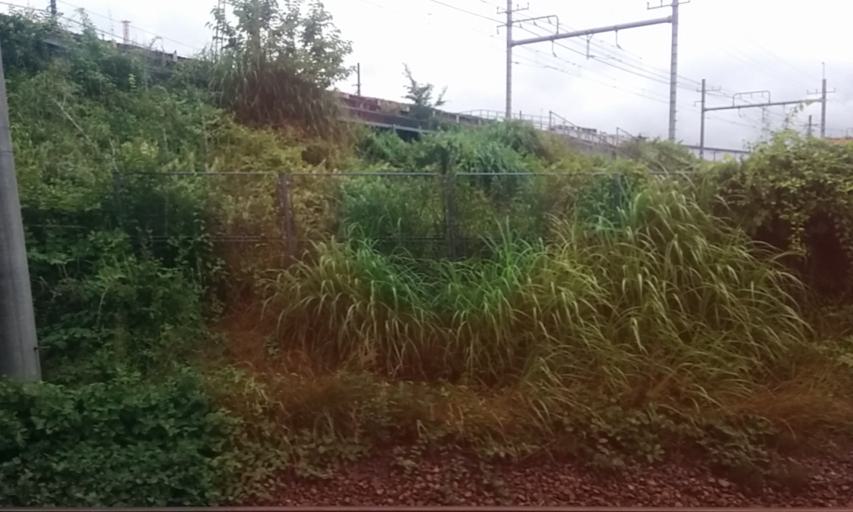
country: JP
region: Tokyo
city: Hachioji
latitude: 35.6539
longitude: 139.3472
